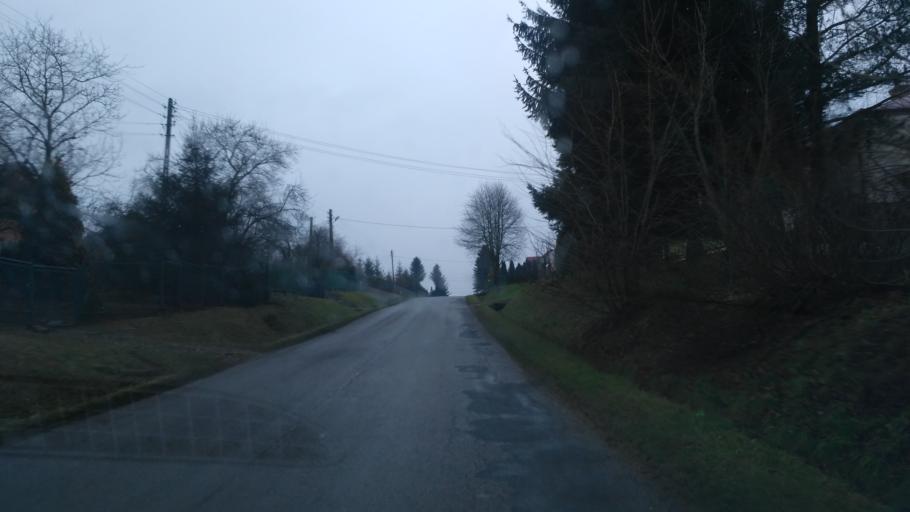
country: PL
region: Subcarpathian Voivodeship
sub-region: Powiat jaroslawski
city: Rokietnica
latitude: 49.9465
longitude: 22.6079
